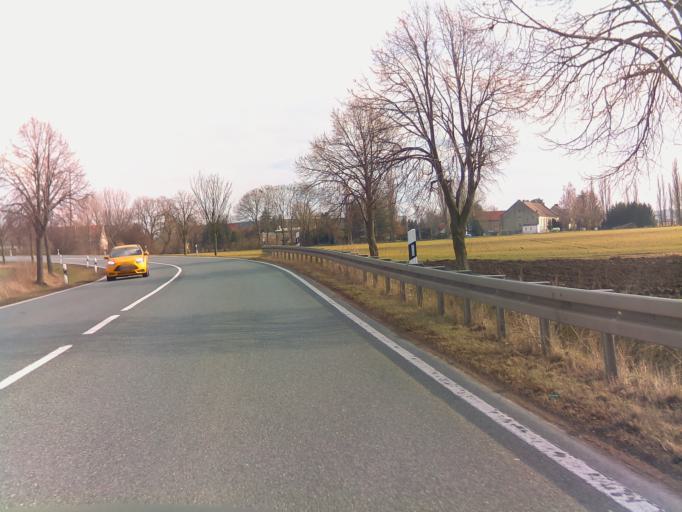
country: DE
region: Saxony-Anhalt
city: Osterfeld
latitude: 51.0985
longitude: 11.9406
